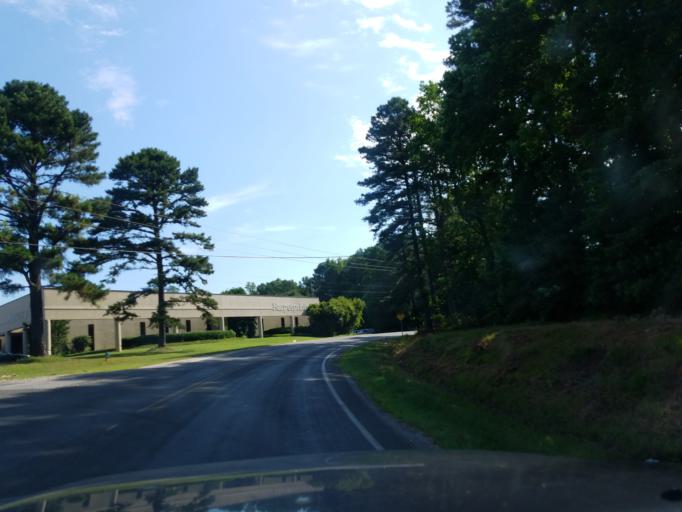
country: US
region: North Carolina
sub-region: Vance County
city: Henderson
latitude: 36.3393
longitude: -78.4377
